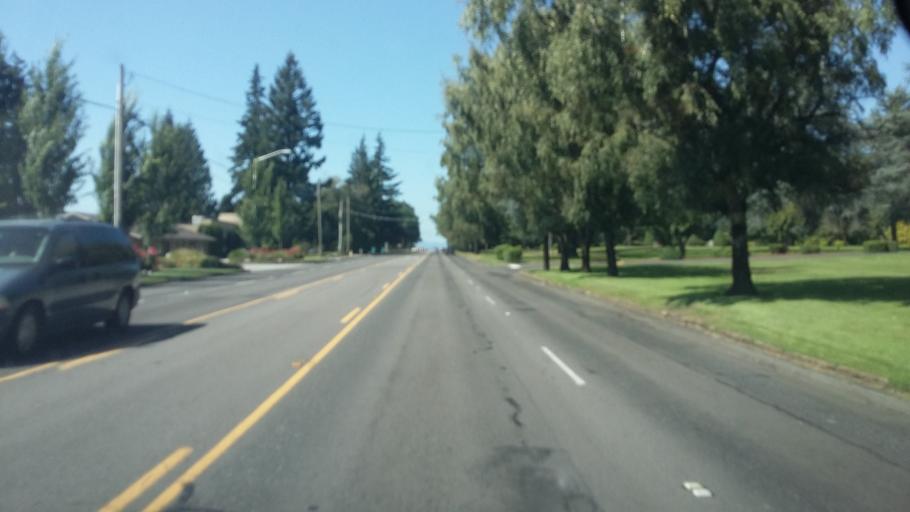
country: US
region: Washington
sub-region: Clark County
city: Orchards
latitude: 45.6294
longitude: -122.5577
